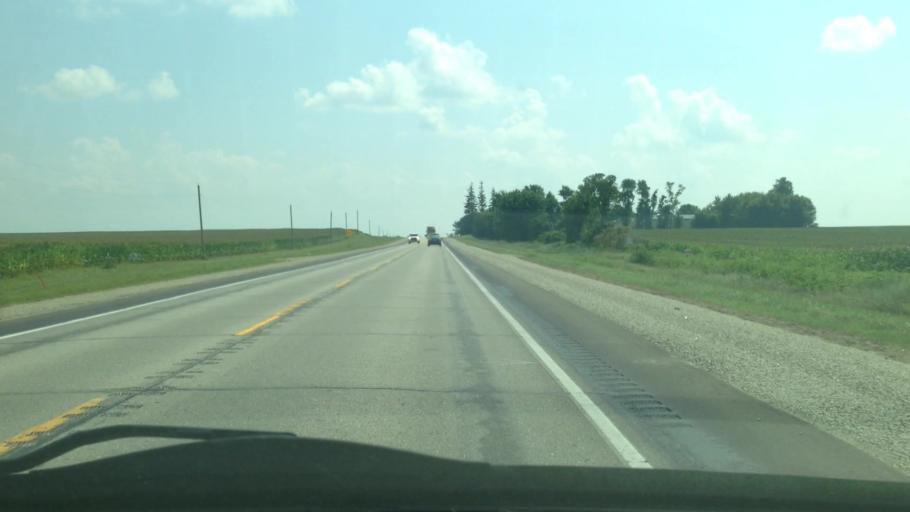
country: US
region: Iowa
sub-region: Howard County
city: Cresco
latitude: 43.4096
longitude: -92.2987
